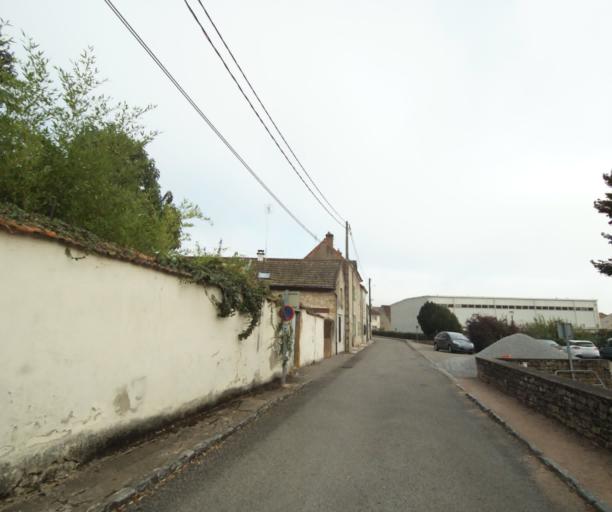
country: FR
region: Bourgogne
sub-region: Departement de Saone-et-Loire
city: Charolles
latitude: 46.4335
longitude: 4.2722
